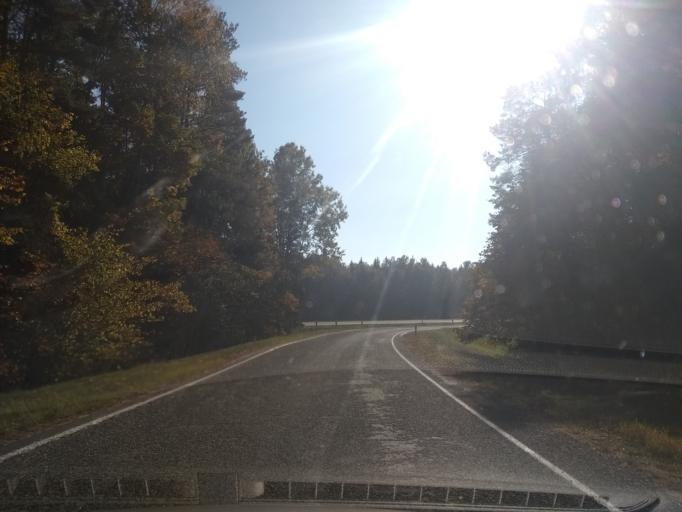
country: BY
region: Brest
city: Ivatsevichy
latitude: 52.8542
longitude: 25.6423
